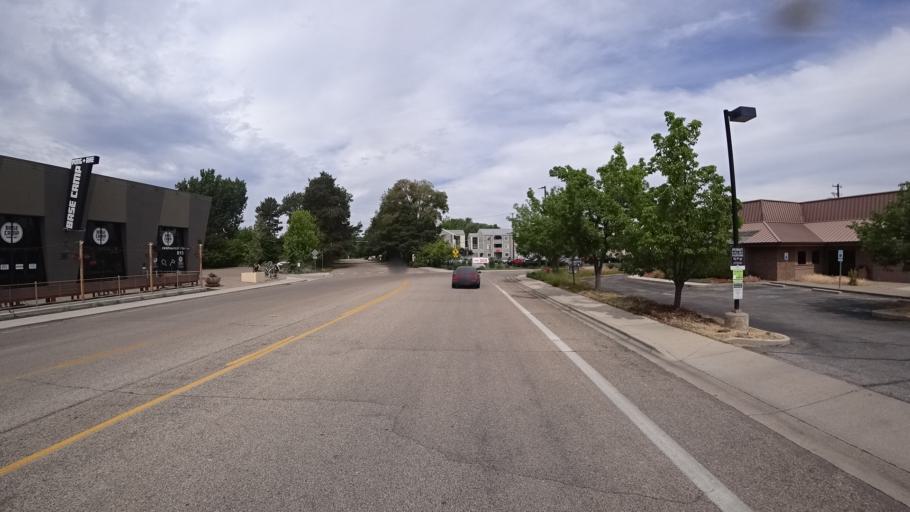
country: US
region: Idaho
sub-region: Ada County
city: Boise
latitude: 43.6061
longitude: -116.2124
